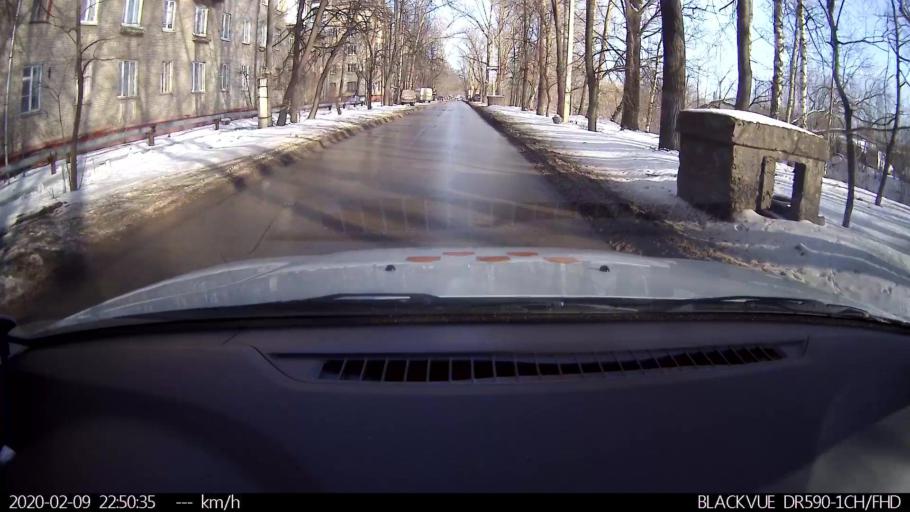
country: RU
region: Nizjnij Novgorod
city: Nizhniy Novgorod
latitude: 56.2627
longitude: 43.9124
